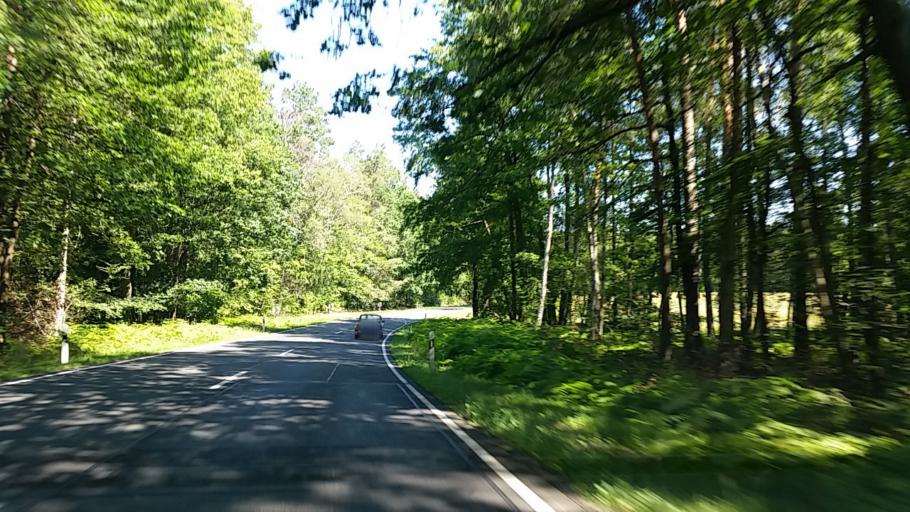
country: DE
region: Saxony-Anhalt
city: Kemberg
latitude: 51.6888
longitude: 12.6130
